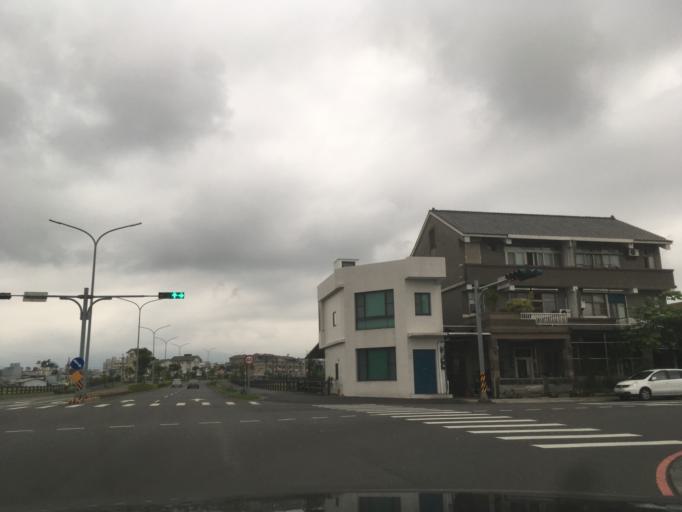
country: TW
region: Taiwan
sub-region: Yilan
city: Yilan
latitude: 24.7378
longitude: 121.7502
